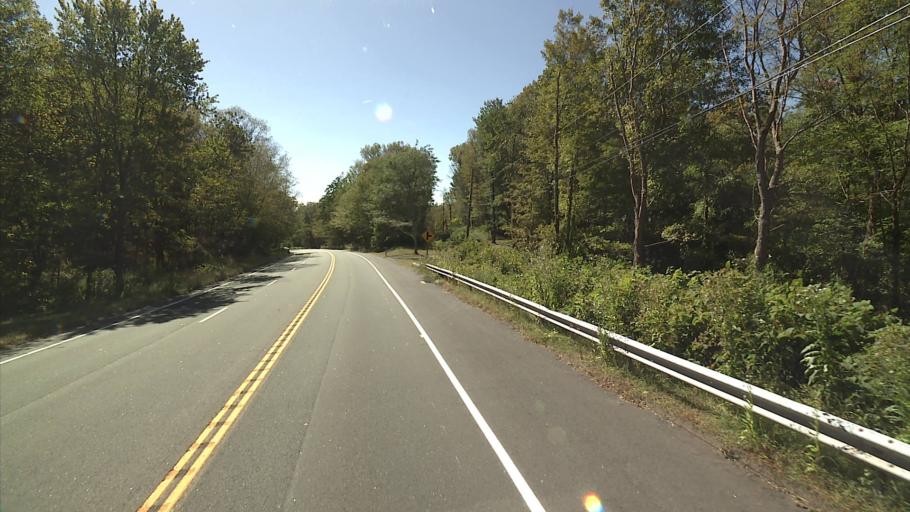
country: US
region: Connecticut
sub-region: New Haven County
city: Woodbridge
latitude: 41.3978
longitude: -72.9744
